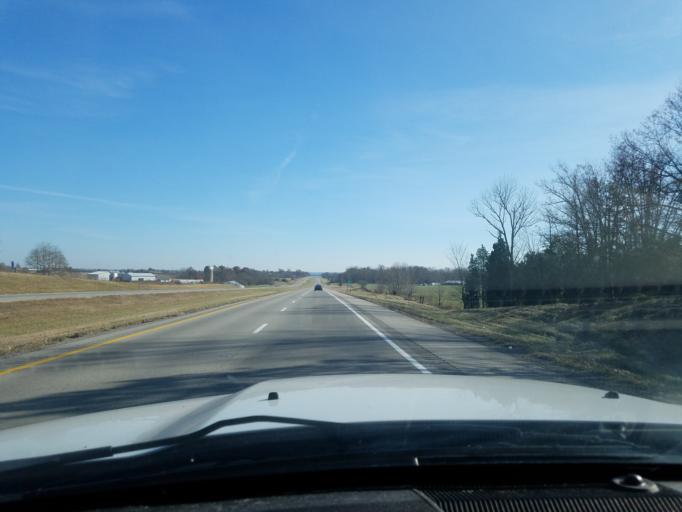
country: US
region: Ohio
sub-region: Adams County
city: Winchester
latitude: 38.9333
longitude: -83.6061
